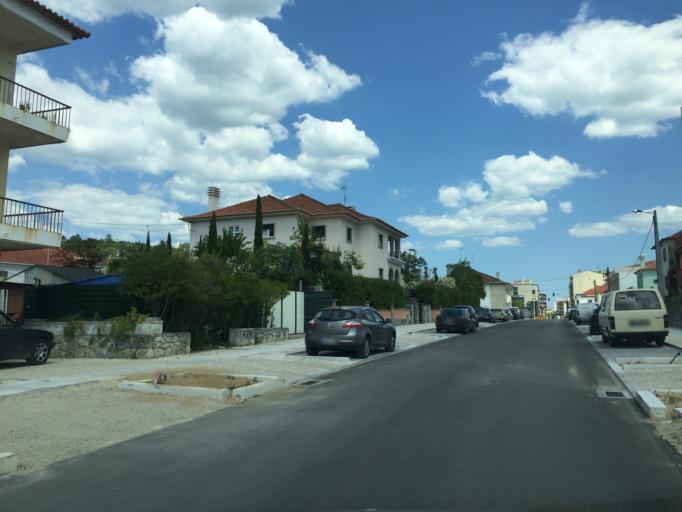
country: PT
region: Santarem
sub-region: Ourem
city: Ourem
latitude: 39.6566
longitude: -8.5819
